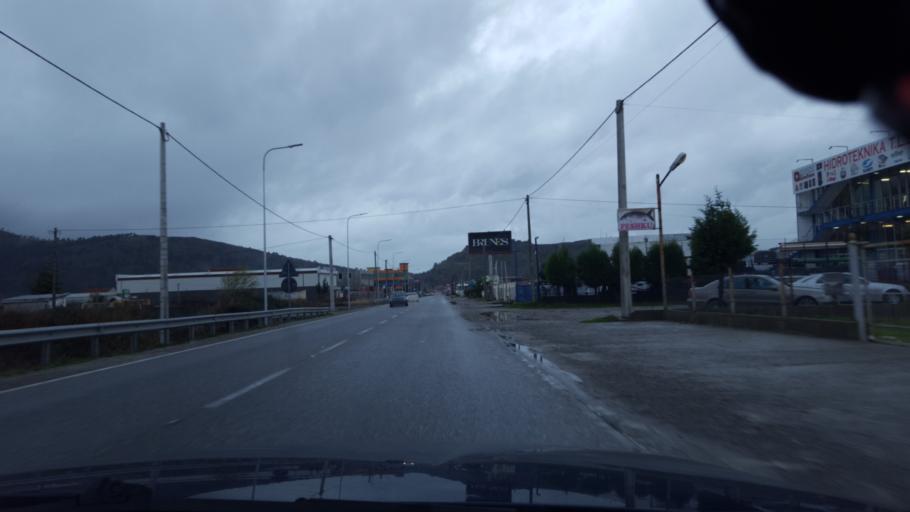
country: AL
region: Shkoder
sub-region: Rrethi i Malesia e Madhe
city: Kuc
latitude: 42.0337
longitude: 19.5017
